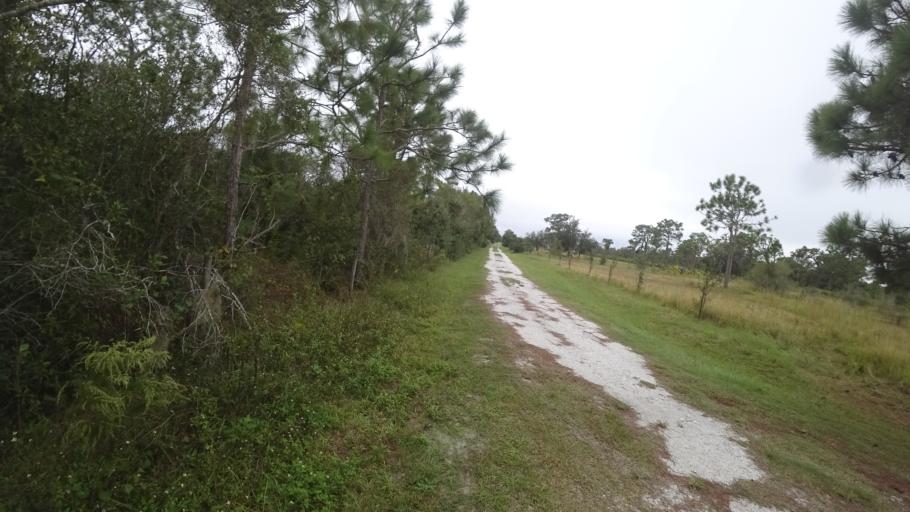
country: US
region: Florida
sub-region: Sarasota County
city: Warm Mineral Springs
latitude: 27.2774
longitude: -82.1327
